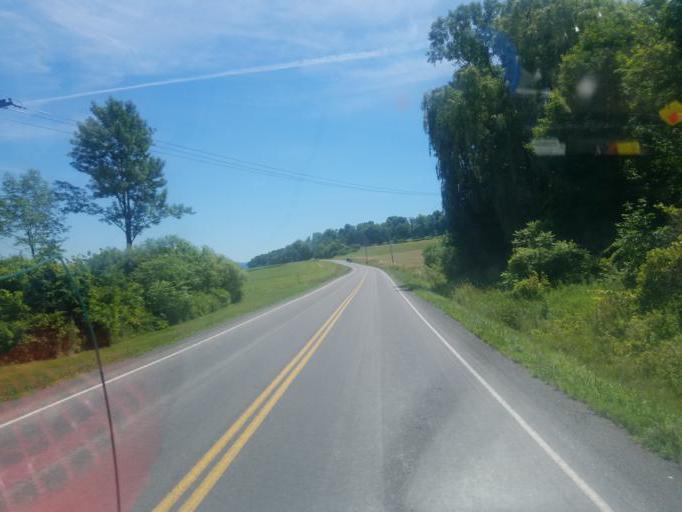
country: US
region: New York
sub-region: Yates County
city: Dundee
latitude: 42.6018
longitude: -76.9680
